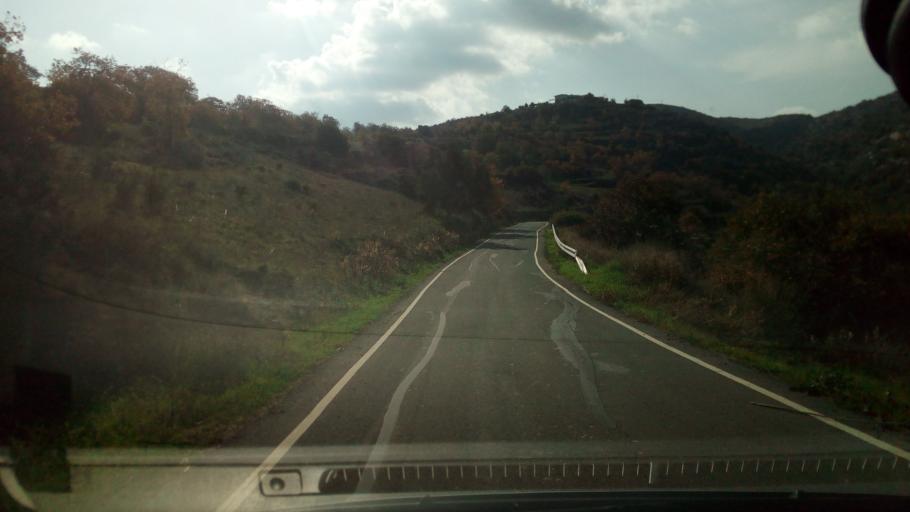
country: CY
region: Pafos
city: Polis
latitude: 34.9556
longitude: 32.4294
